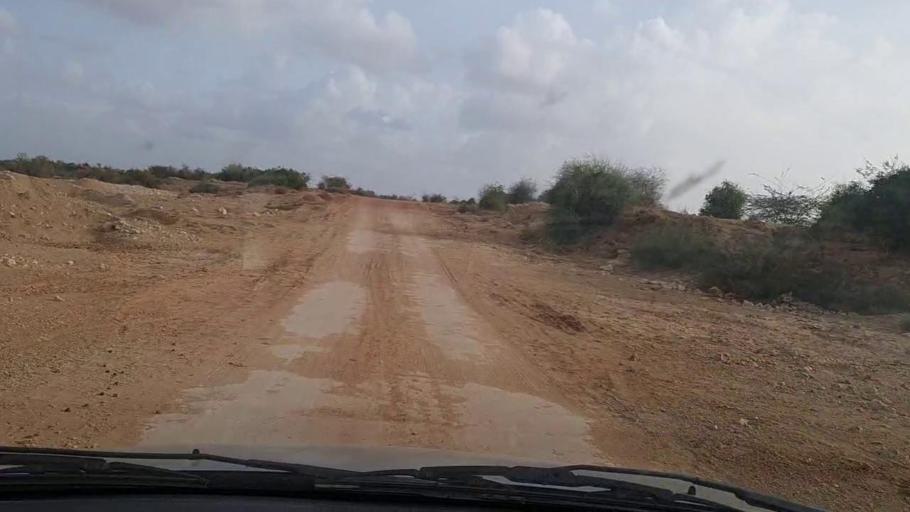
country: PK
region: Sindh
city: Thatta
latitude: 25.0722
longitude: 67.8903
